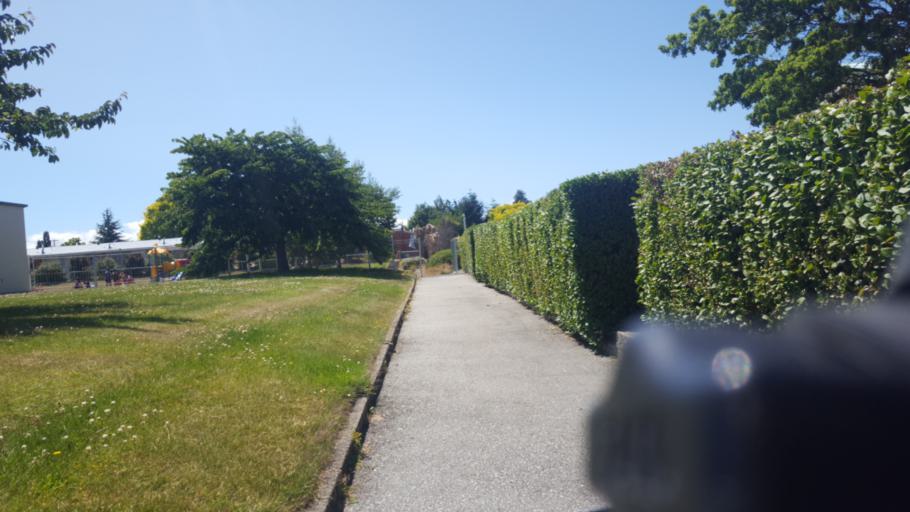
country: NZ
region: Otago
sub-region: Dunedin City
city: Dunedin
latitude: -45.1297
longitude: 170.1025
